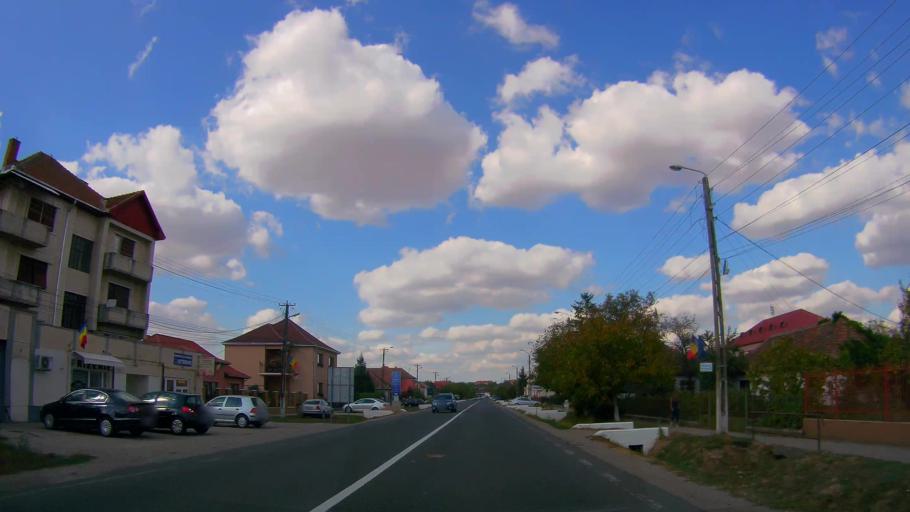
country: RO
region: Satu Mare
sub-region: Oras Ardud
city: Ardud
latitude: 47.6456
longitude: 22.8914
